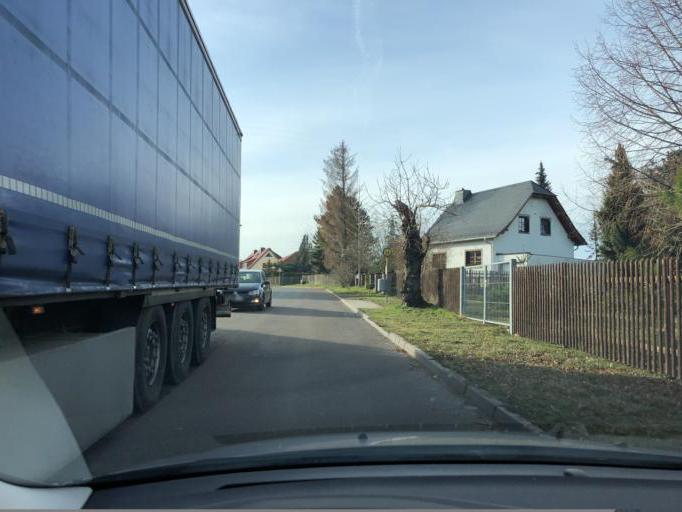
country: DE
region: Saxony-Anhalt
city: Reichardtswerben
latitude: 51.2429
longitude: 11.9506
